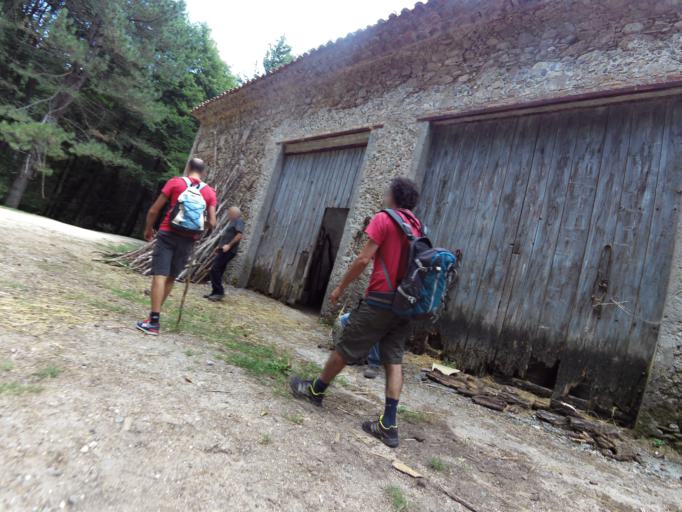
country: IT
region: Calabria
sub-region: Provincia di Vibo-Valentia
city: Nardodipace
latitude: 38.5095
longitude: 16.3787
